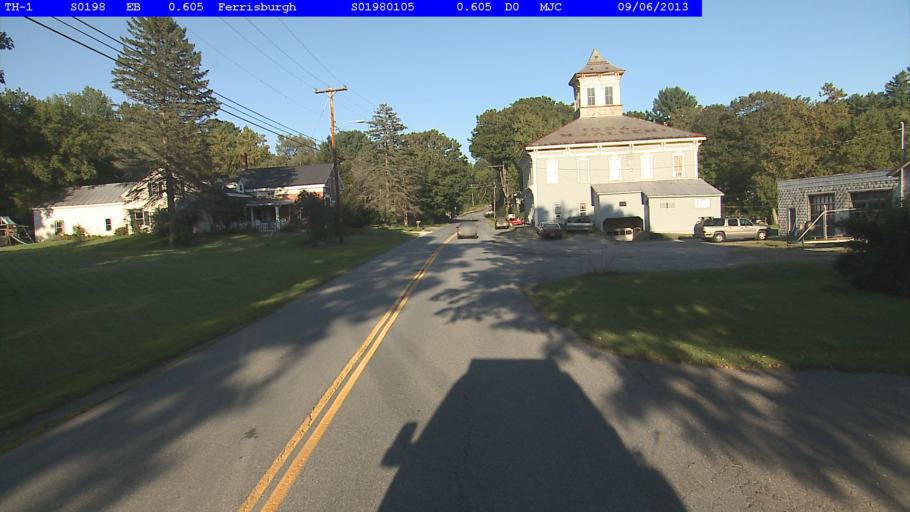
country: US
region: Vermont
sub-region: Addison County
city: Vergennes
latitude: 44.2591
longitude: -73.2161
